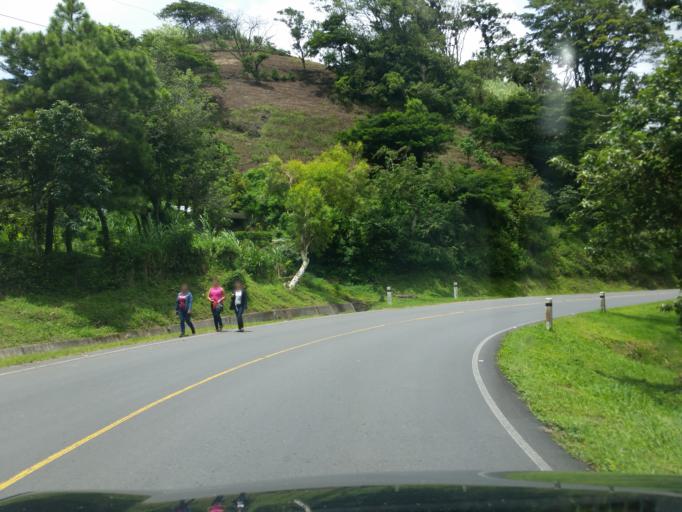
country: NI
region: Matagalpa
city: Matagalpa
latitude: 12.9943
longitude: -85.9223
